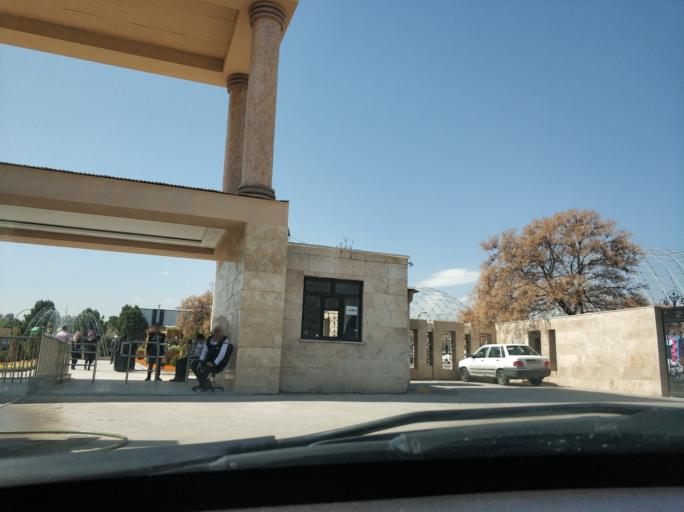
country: IR
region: Razavi Khorasan
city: Mashhad
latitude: 36.2552
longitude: 59.6109
